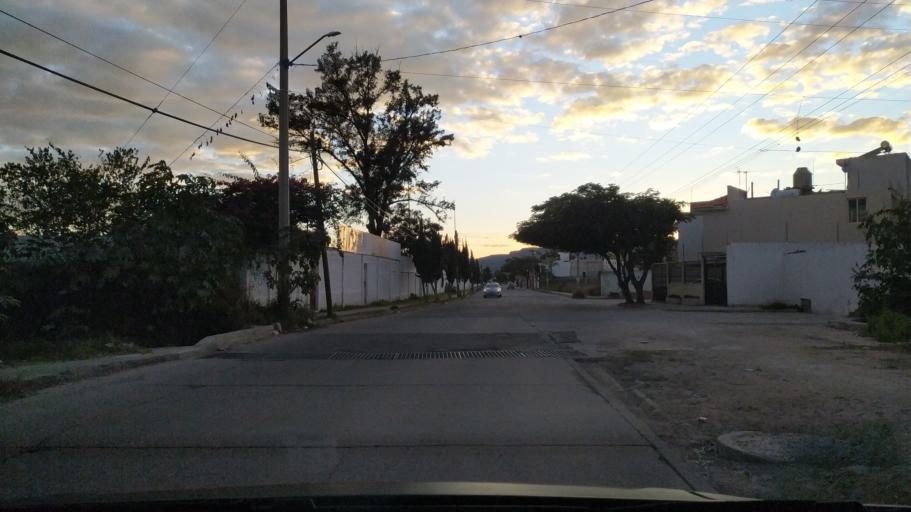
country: MX
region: Guanajuato
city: San Francisco del Rincon
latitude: 21.0323
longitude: -101.8492
